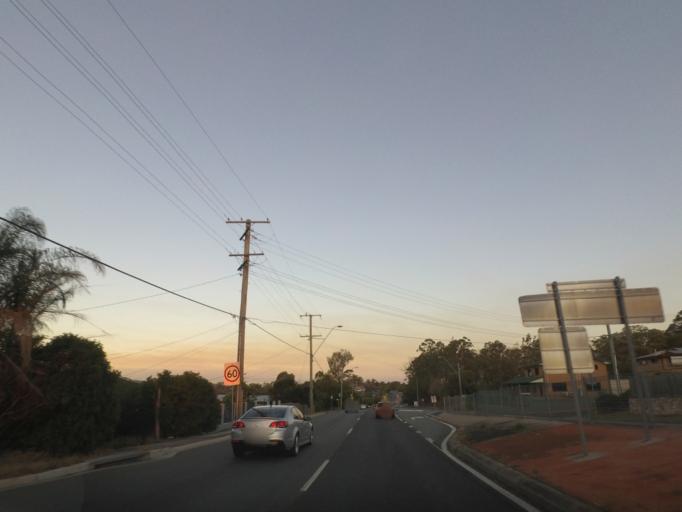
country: AU
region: Queensland
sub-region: Brisbane
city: Upper Mount Gravatt
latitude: -27.5550
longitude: 153.0922
